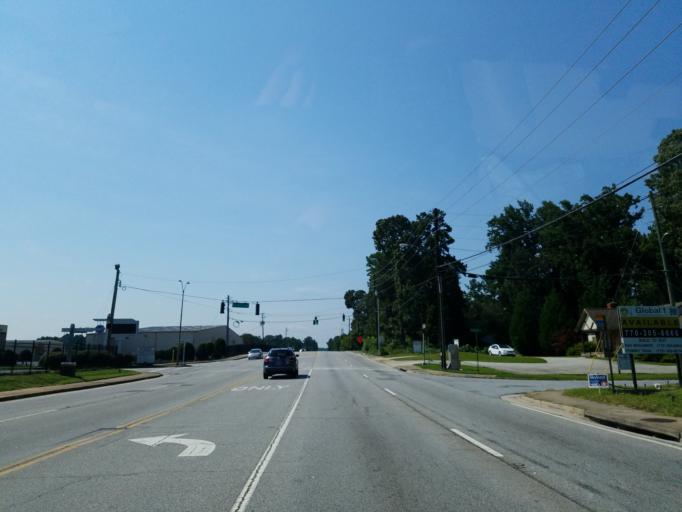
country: US
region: Georgia
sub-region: DeKalb County
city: Chamblee
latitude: 33.8770
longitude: -84.3095
